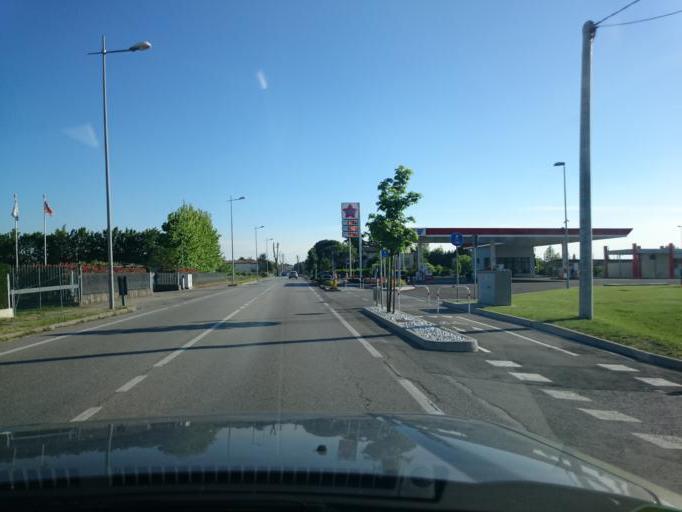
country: IT
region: Veneto
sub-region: Provincia di Padova
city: Vigonza
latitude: 45.4496
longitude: 11.9886
